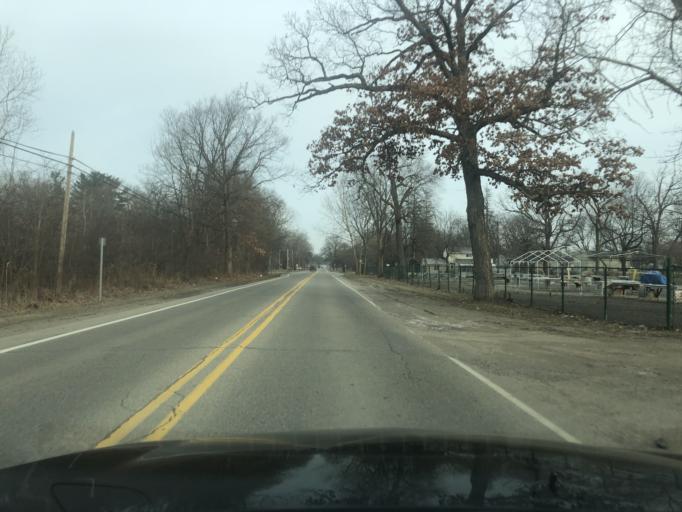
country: US
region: Michigan
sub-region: Wayne County
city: Taylor
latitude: 42.1835
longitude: -83.3256
